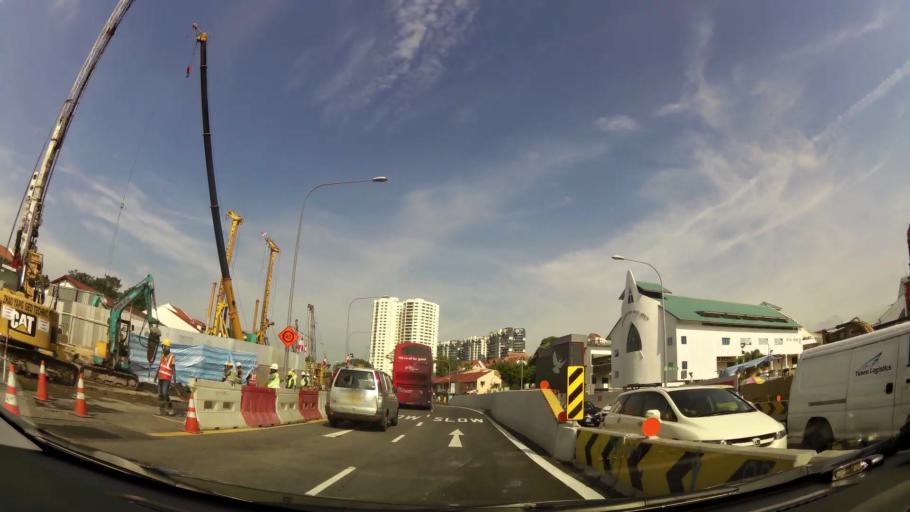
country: SG
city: Singapore
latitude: 1.3538
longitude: 103.8338
